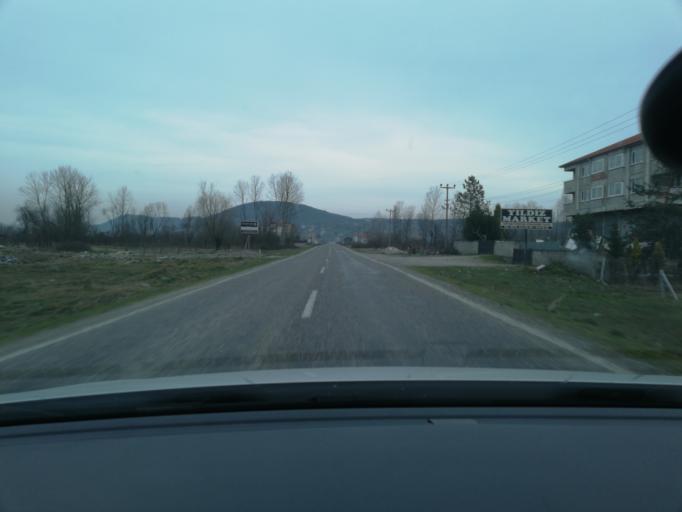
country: TR
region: Zonguldak
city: Saltukova
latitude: 41.5155
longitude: 32.1030
